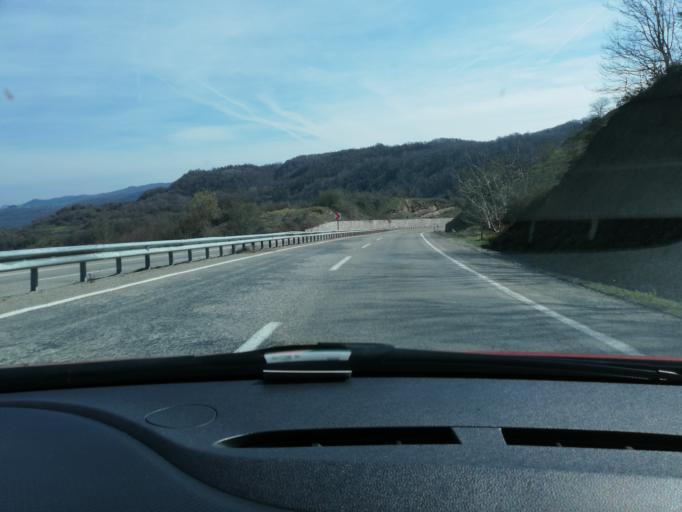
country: TR
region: Bartin
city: Amasra
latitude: 41.7307
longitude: 32.4135
